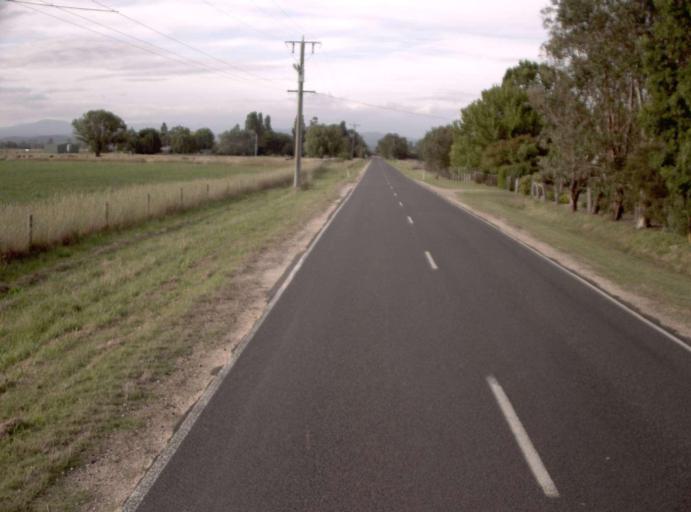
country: AU
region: Victoria
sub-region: Wellington
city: Heyfield
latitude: -37.8921
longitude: 146.9906
